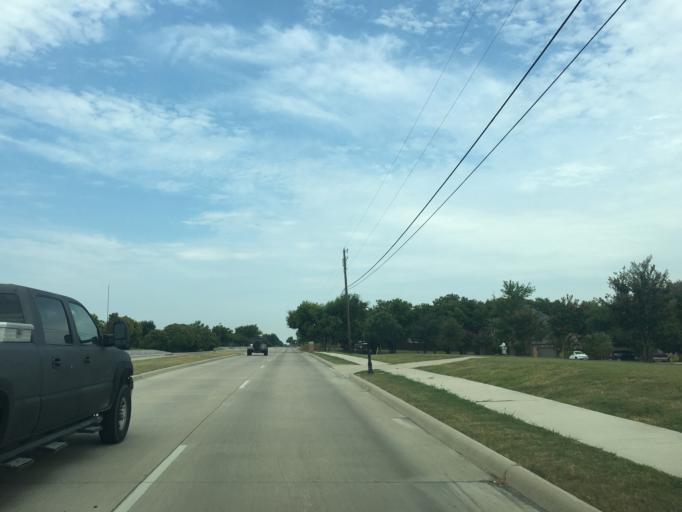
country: US
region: Texas
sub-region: Collin County
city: Wylie
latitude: 33.0059
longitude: -96.5250
